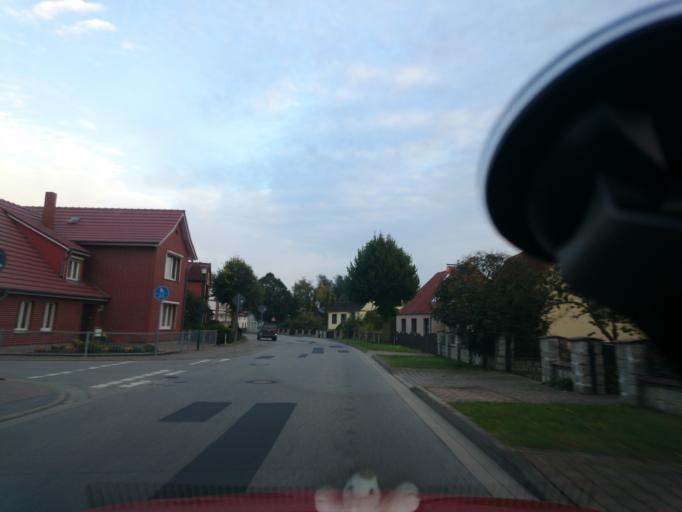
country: DE
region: Mecklenburg-Vorpommern
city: Saal
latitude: 54.3089
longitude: 12.4985
